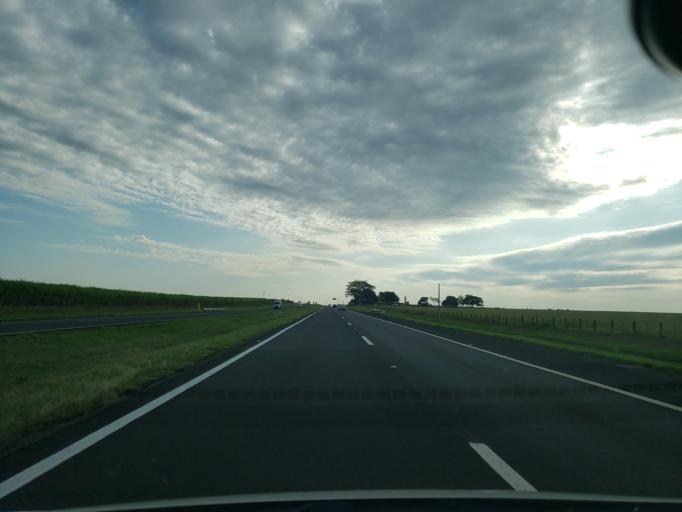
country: BR
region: Sao Paulo
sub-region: Guararapes
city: Guararapes
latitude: -21.2132
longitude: -50.7072
